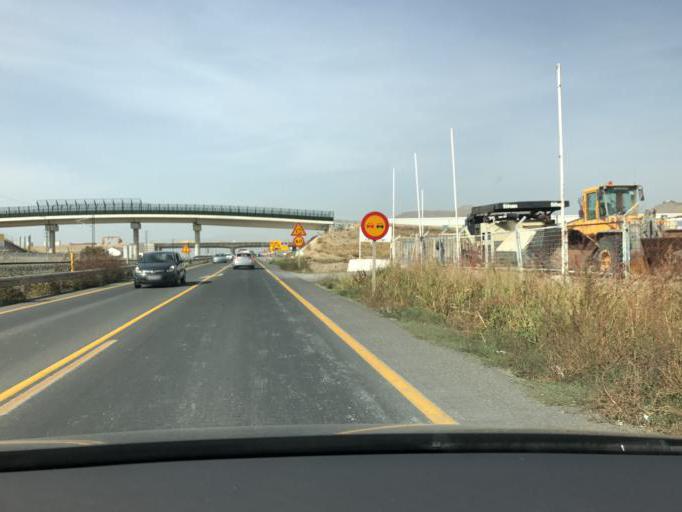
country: ES
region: Andalusia
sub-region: Provincia de Granada
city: Atarfe
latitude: 37.2064
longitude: -3.6713
